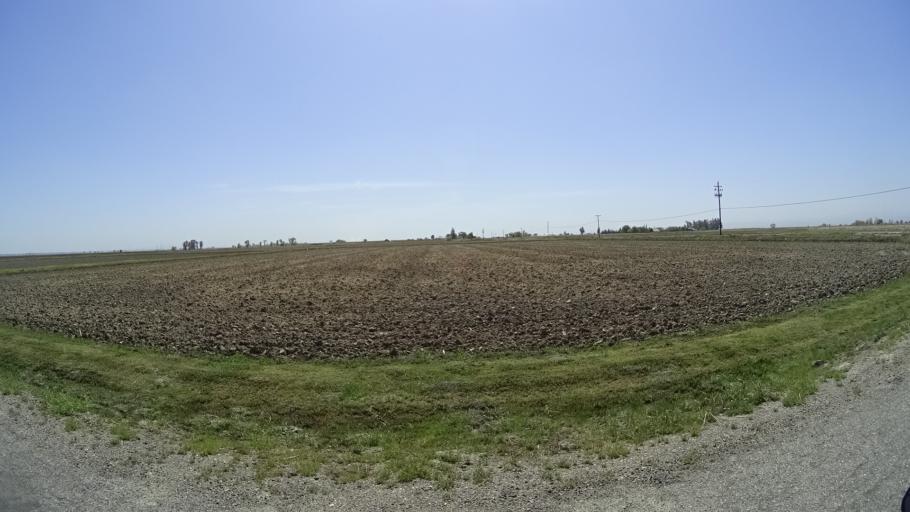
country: US
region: California
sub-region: Glenn County
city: Willows
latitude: 39.5311
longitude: -122.1114
